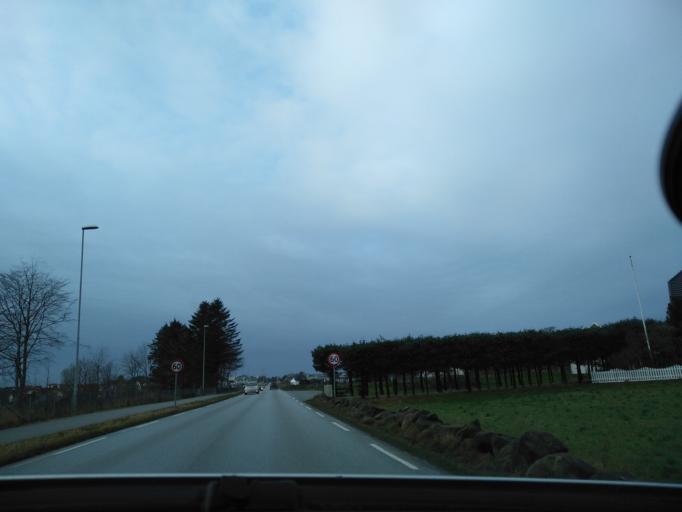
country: NO
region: Rogaland
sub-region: Randaberg
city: Randaberg
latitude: 58.9933
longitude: 5.6440
